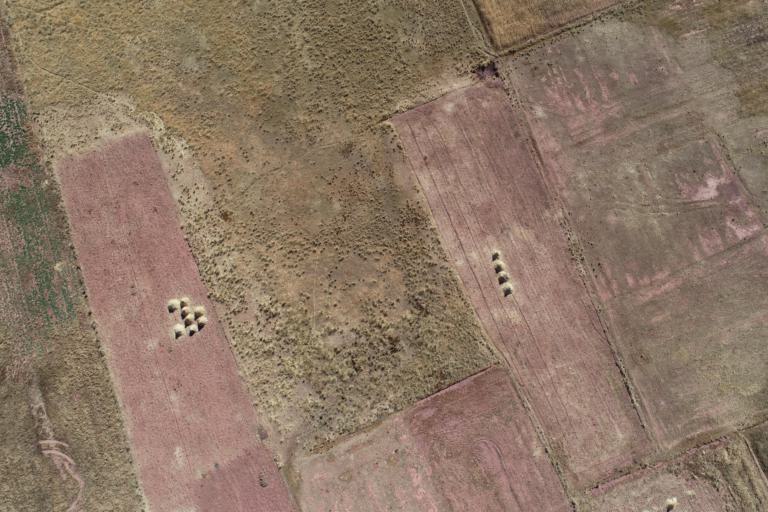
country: BO
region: La Paz
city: Tiahuanaco
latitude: -16.5920
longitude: -68.7564
